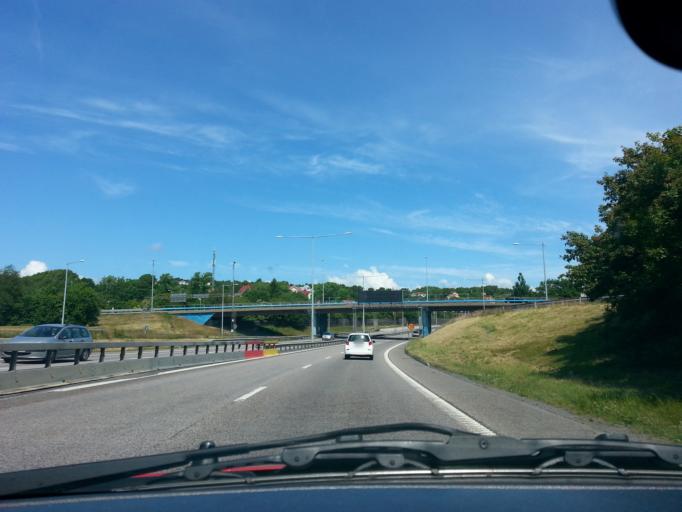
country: SE
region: Vaestra Goetaland
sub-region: Goteborg
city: Majorna
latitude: 57.6764
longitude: 11.8958
